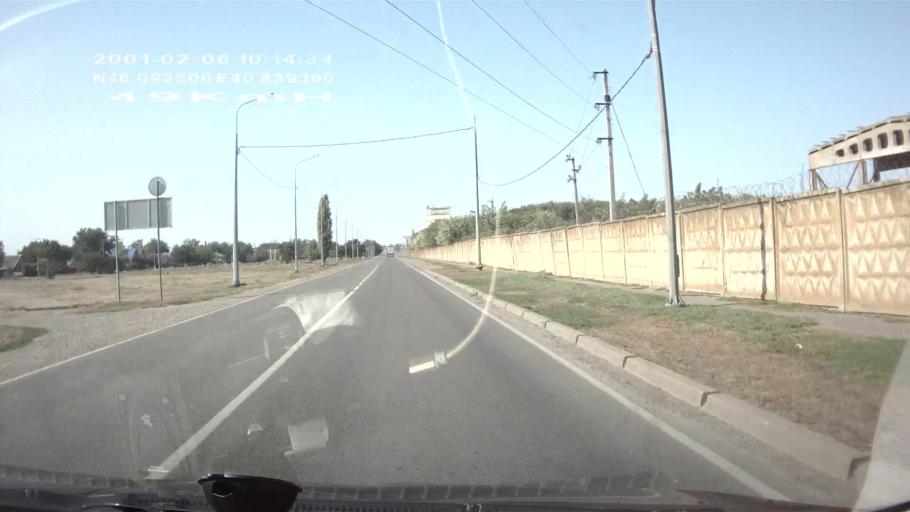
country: RU
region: Krasnodarskiy
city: Belaya Glina
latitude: 46.0924
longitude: 40.8393
